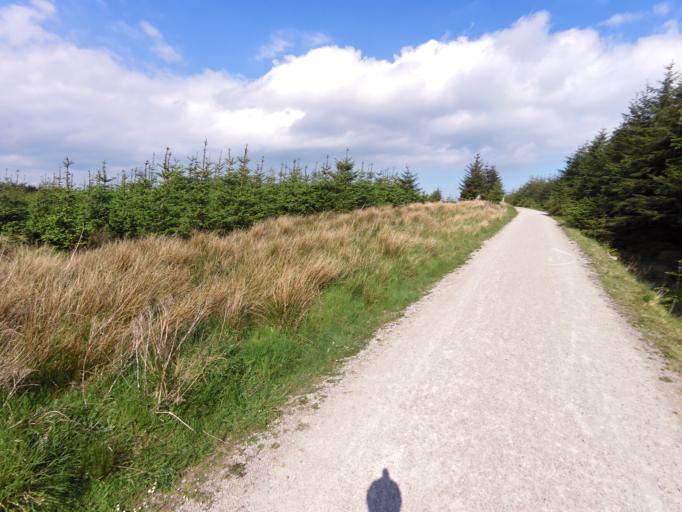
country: GB
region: England
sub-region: North Yorkshire
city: Settle
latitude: 54.0172
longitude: -2.3701
